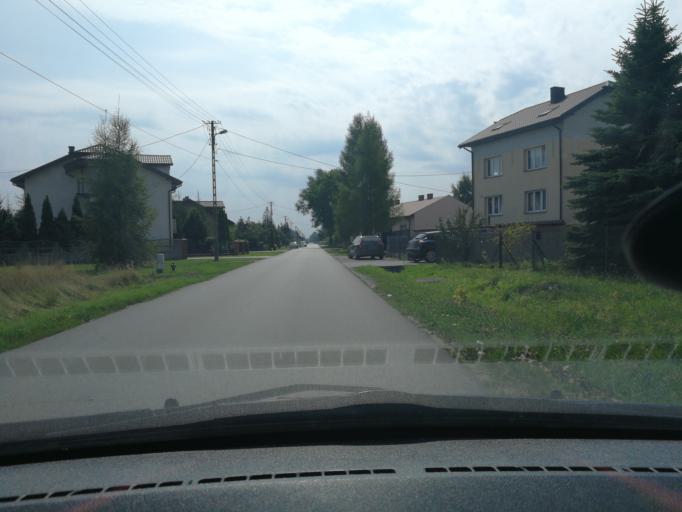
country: PL
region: Lodz Voivodeship
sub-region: Powiat skierniewicki
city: Makow
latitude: 52.0059
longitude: 20.0707
